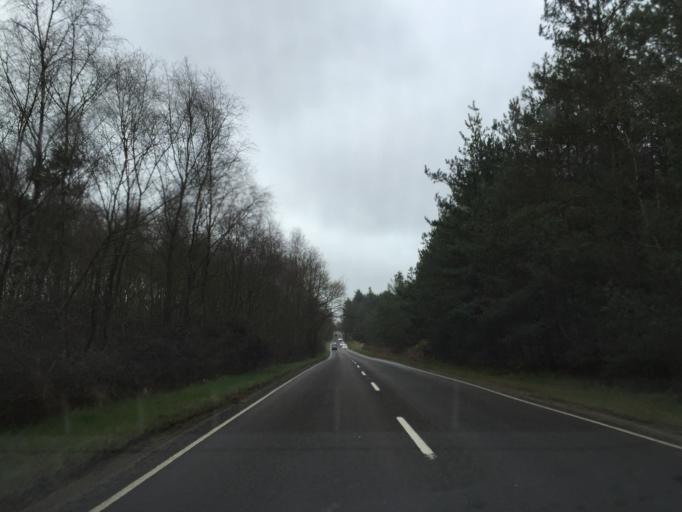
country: GB
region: England
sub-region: Dorset
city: St Leonards
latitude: 50.8582
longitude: -1.8278
